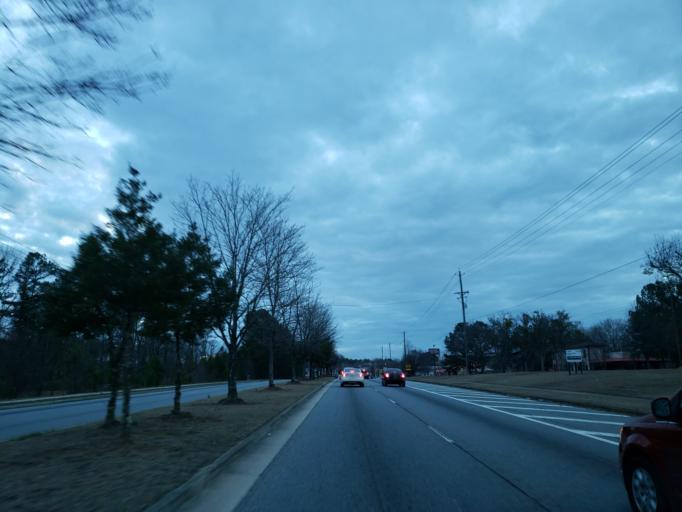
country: US
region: Georgia
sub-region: Cobb County
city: Mableton
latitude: 33.8553
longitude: -84.5942
